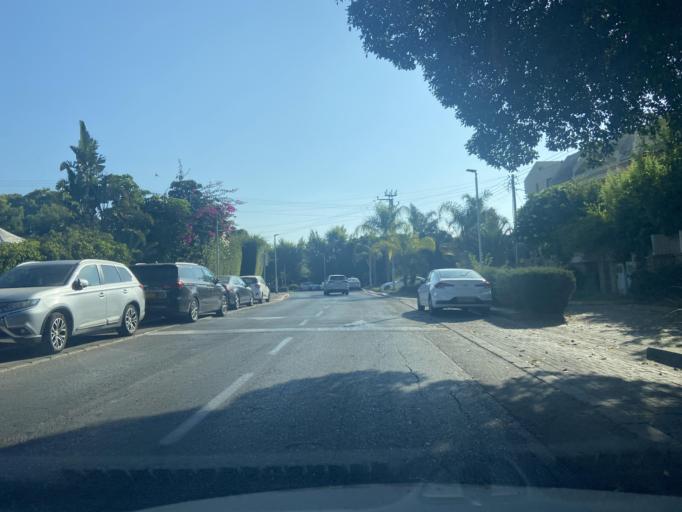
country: IL
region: Central District
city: Yehud
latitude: 32.0386
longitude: 34.8933
